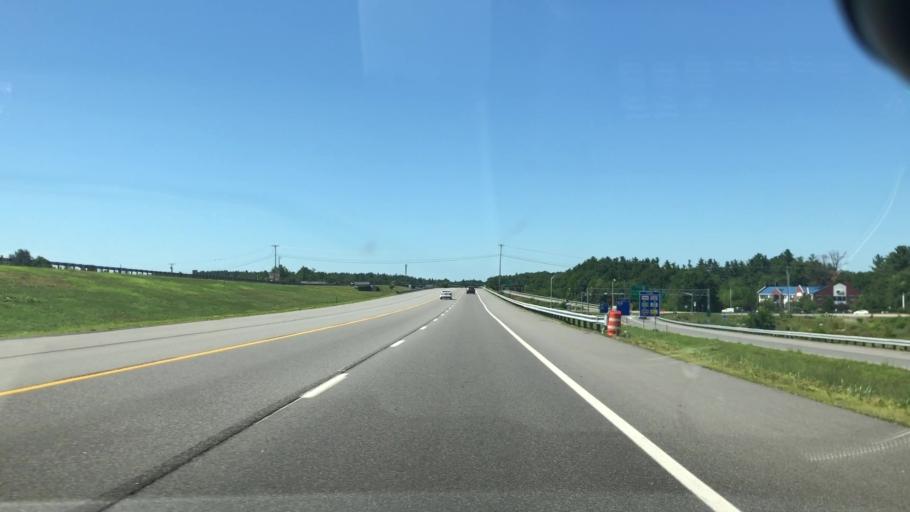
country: US
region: New Hampshire
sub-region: Rockingham County
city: Londonderry
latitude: 42.9139
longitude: -71.3693
